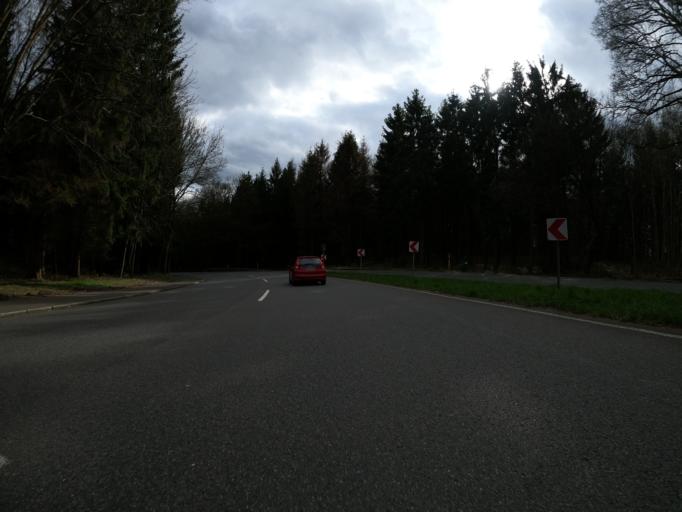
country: DE
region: North Rhine-Westphalia
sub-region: Regierungsbezirk Dusseldorf
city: Solingen
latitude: 51.1990
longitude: 7.1120
